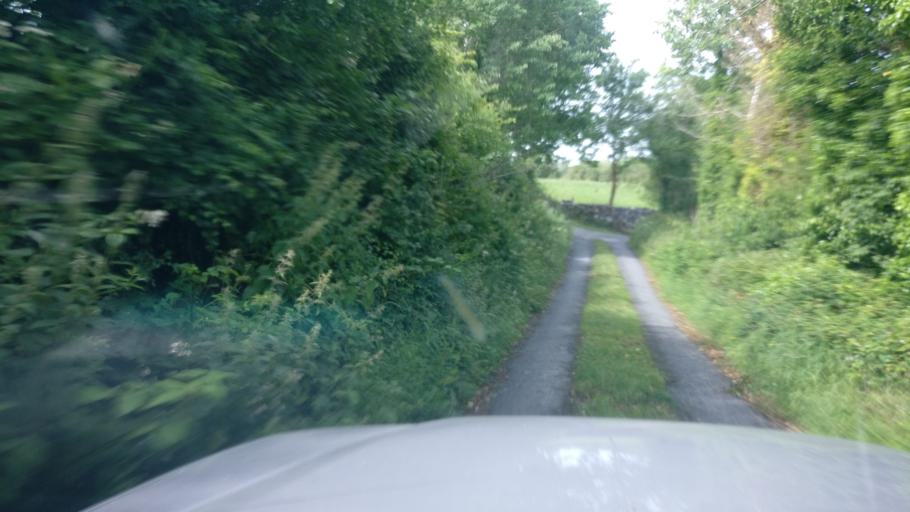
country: IE
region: Connaught
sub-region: County Galway
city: Gort
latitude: 53.0798
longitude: -8.7712
